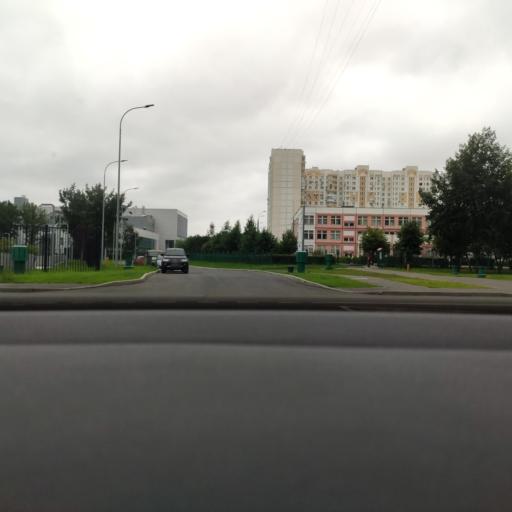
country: RU
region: Moscow
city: Severnyy
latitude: 55.9356
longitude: 37.5542
